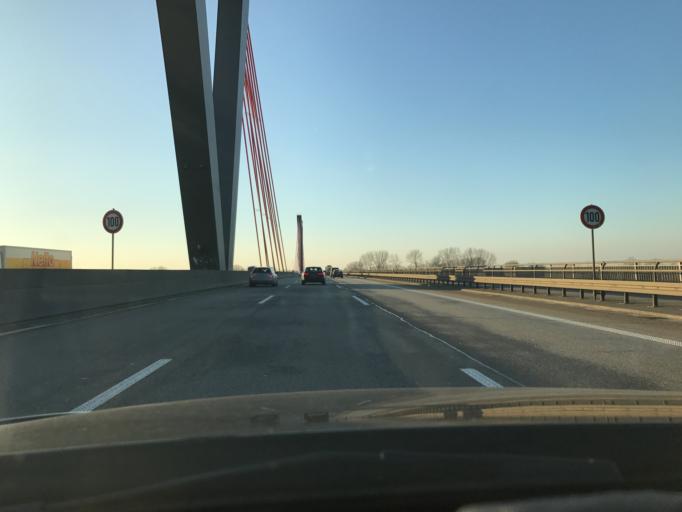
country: DE
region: North Rhine-Westphalia
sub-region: Regierungsbezirk Dusseldorf
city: Meerbusch
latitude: 51.2775
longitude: 6.7072
